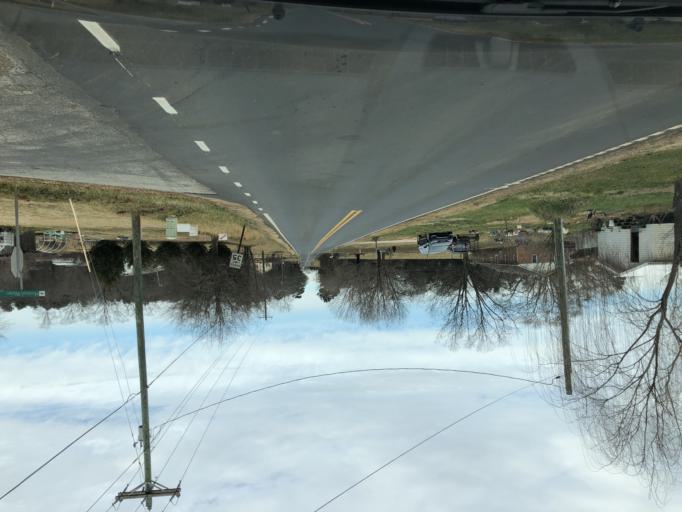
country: US
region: South Carolina
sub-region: Greenville County
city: Five Forks
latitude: 34.8527
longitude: -82.1935
